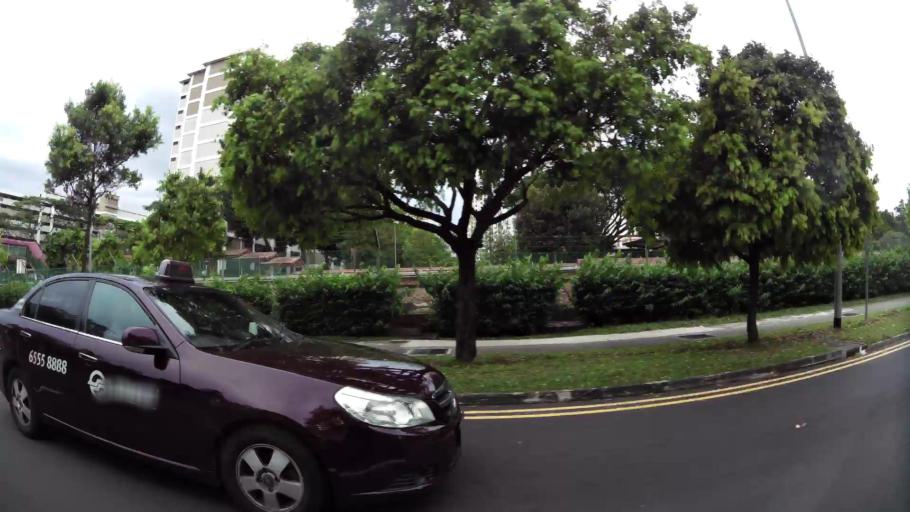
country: SG
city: Singapore
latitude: 1.3721
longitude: 103.8484
